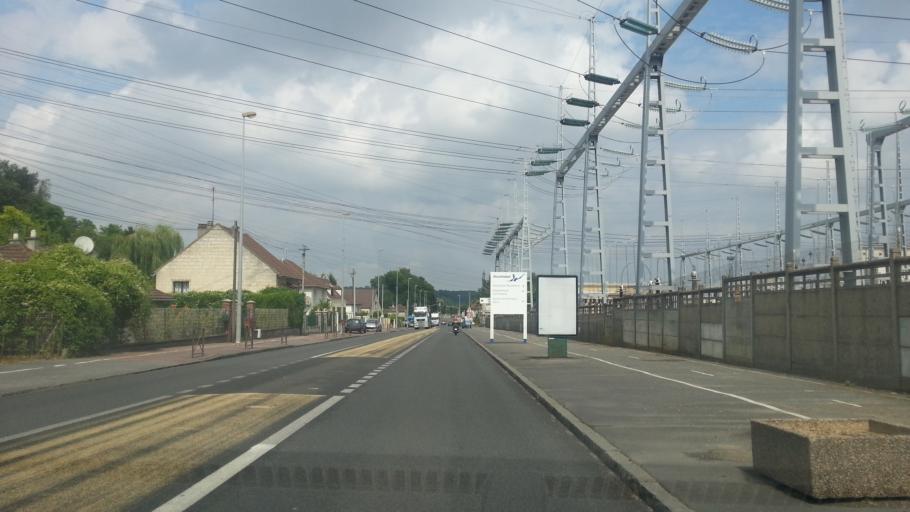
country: FR
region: Picardie
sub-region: Departement de l'Oise
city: Thiverny
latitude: 49.2417
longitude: 2.4398
